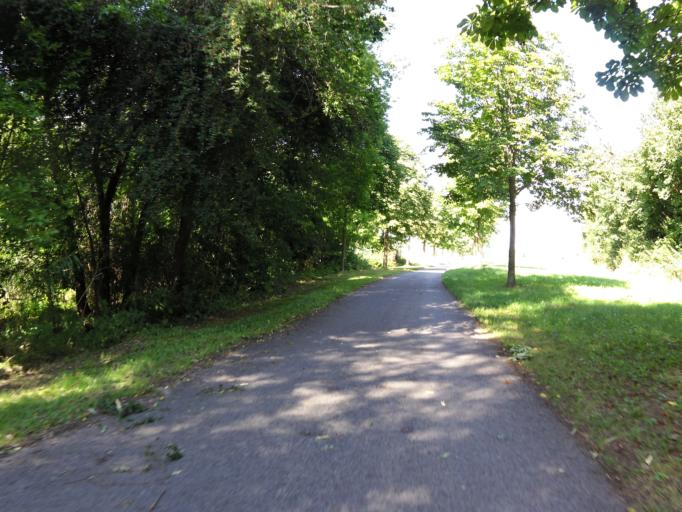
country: DE
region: Bavaria
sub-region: Regierungsbezirk Unterfranken
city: Marktsteft
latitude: 49.7006
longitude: 10.1340
